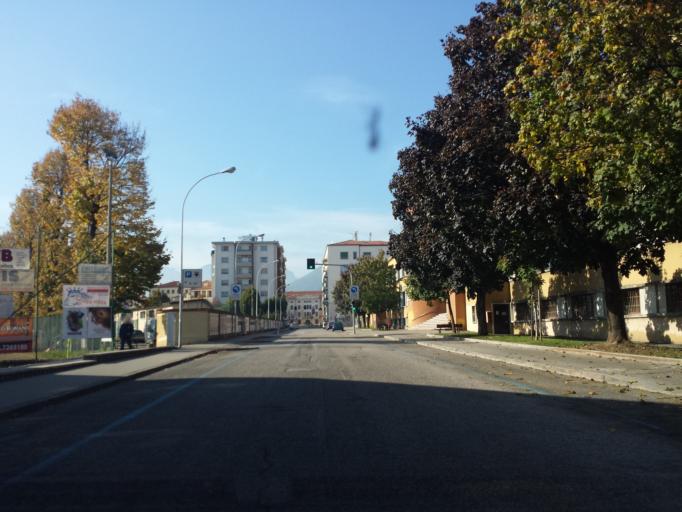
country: IT
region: Veneto
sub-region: Provincia di Vicenza
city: Schio
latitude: 45.7120
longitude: 11.3612
